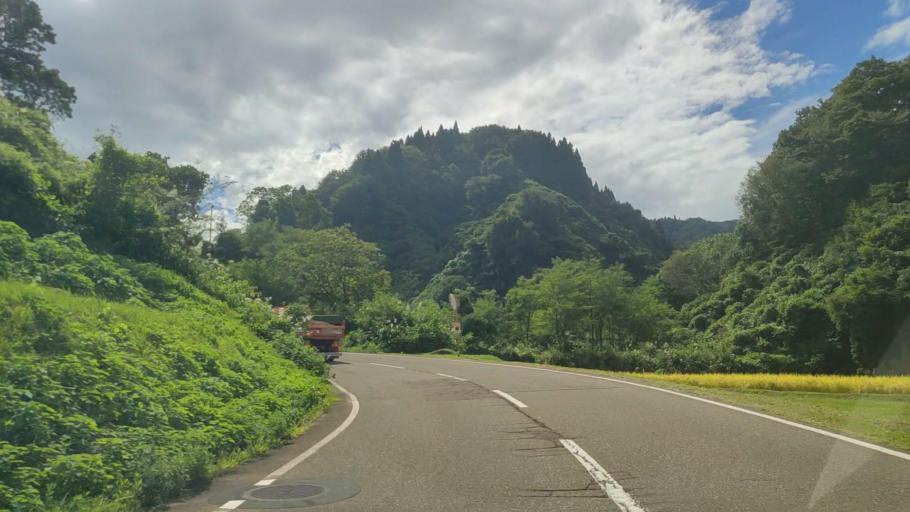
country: JP
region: Niigata
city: Arai
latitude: 36.9408
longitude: 138.2915
